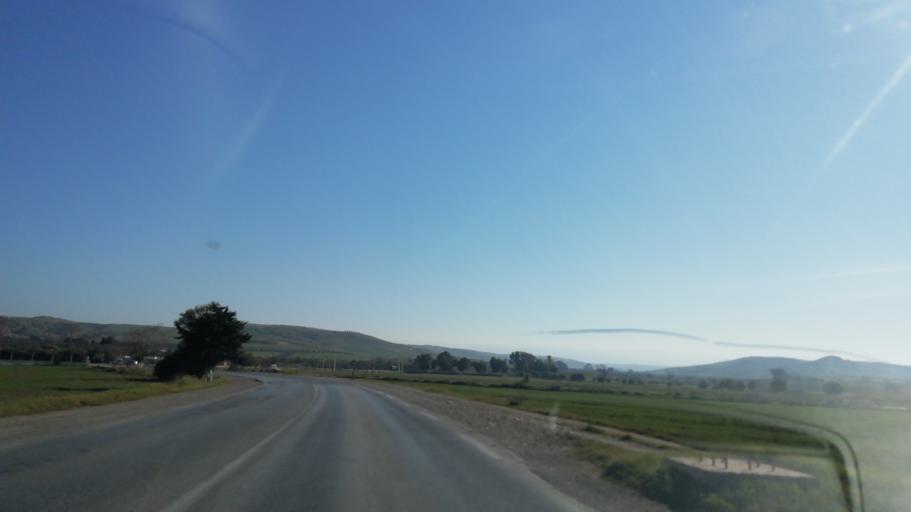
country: DZ
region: Tlemcen
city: Remchi
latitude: 35.0481
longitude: -1.5076
